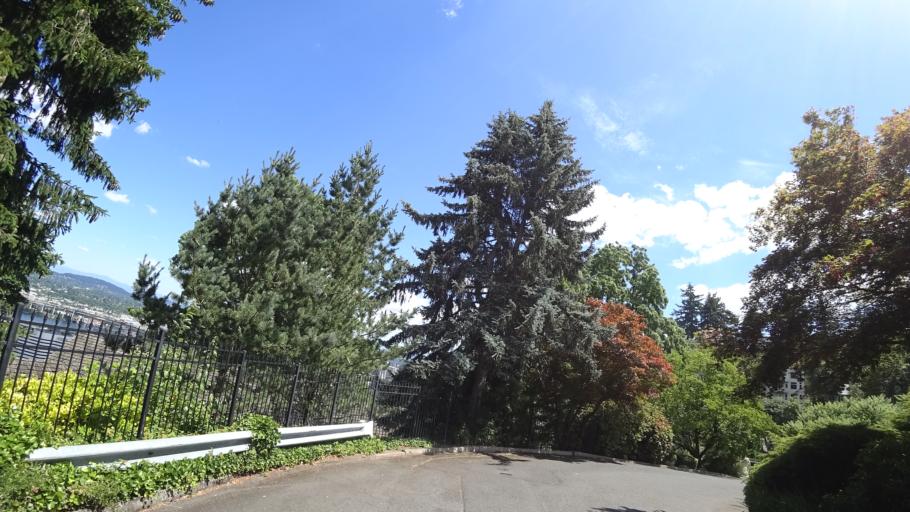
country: US
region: Oregon
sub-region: Multnomah County
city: Portland
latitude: 45.5078
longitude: -122.6888
